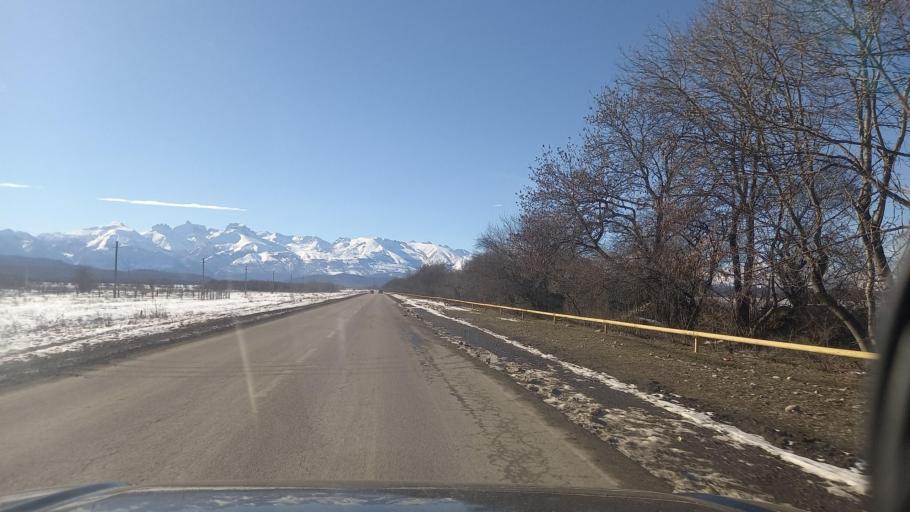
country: RU
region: North Ossetia
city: Chikola
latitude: 43.1834
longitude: 43.8944
